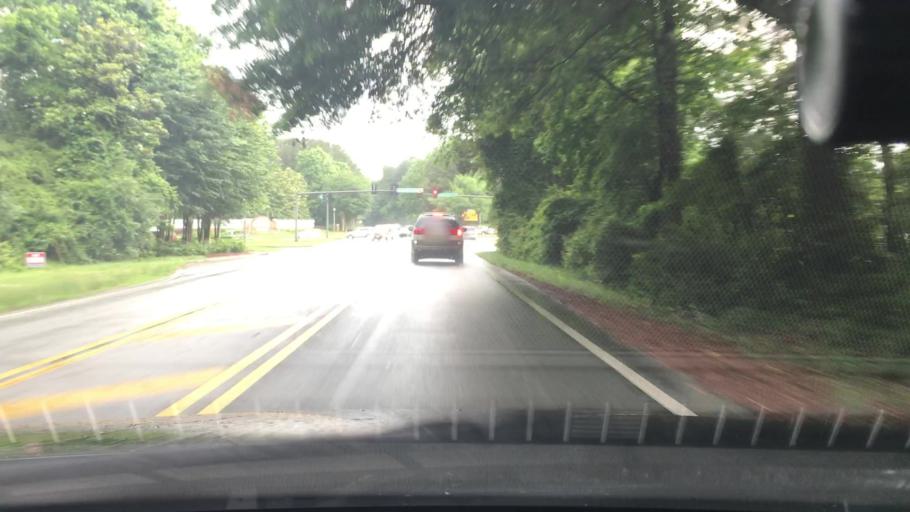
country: US
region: Georgia
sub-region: Coweta County
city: East Newnan
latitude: 33.3794
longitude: -84.7371
